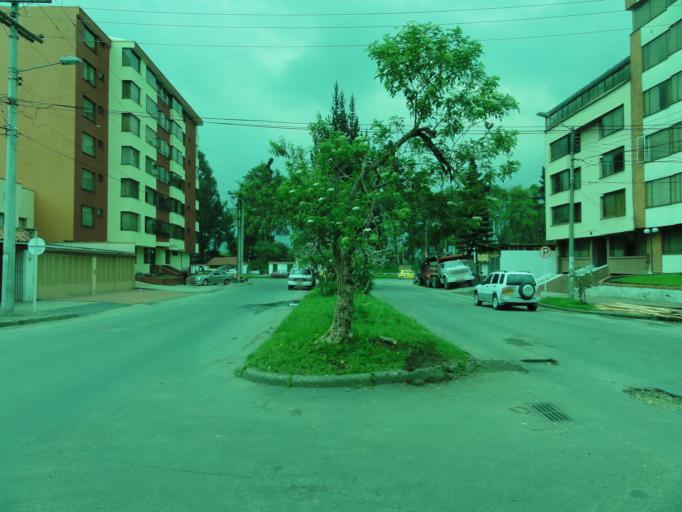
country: CO
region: Bogota D.C.
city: Bogota
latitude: 4.6521
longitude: -74.0825
